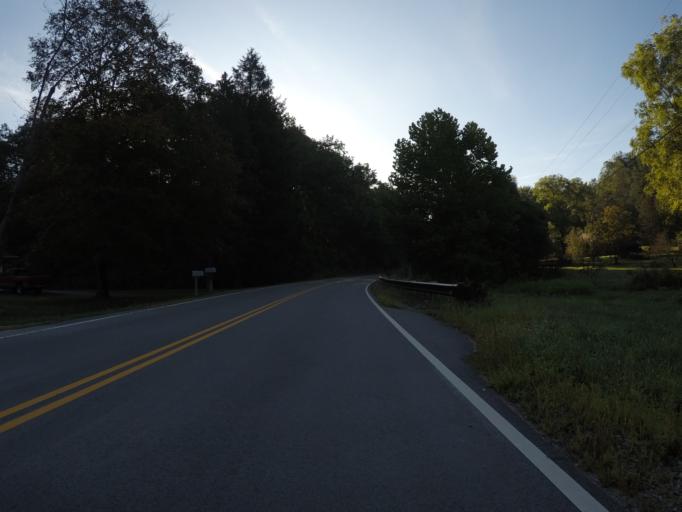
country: US
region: Ohio
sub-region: Lawrence County
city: Coal Grove
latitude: 38.6066
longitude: -82.5761
